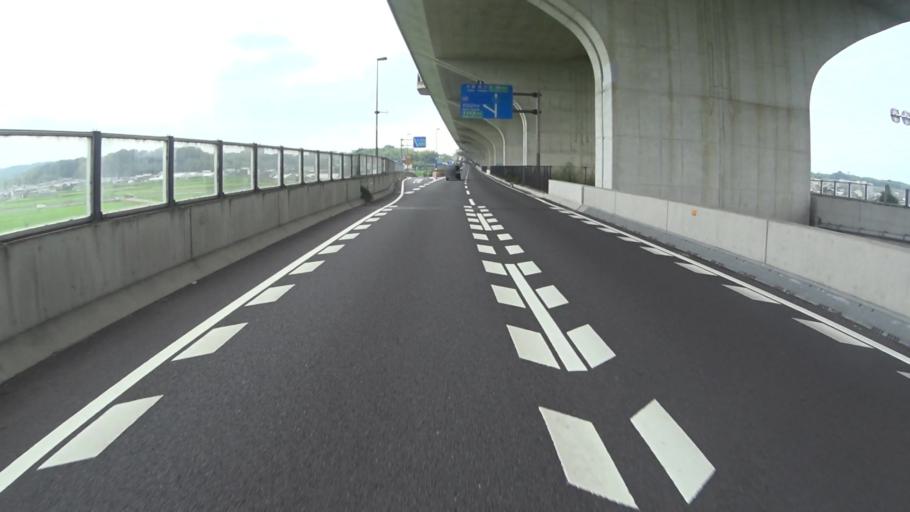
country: JP
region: Kyoto
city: Yawata
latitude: 34.8522
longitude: 135.7330
